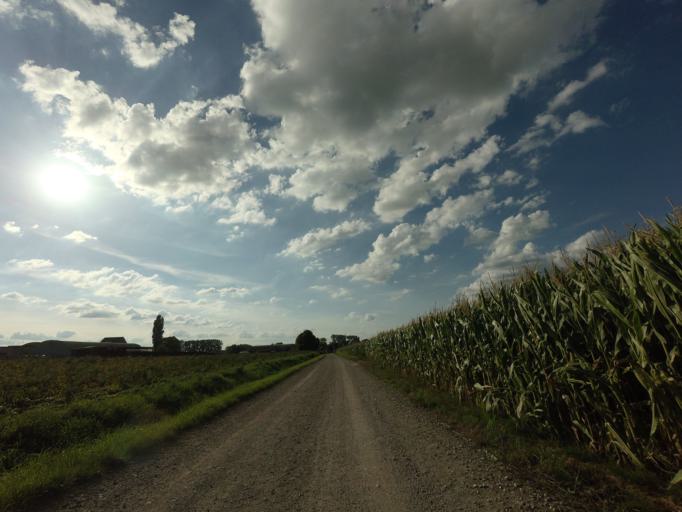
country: BE
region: Flanders
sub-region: Provincie Vlaams-Brabant
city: Meise
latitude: 50.9525
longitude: 4.3326
